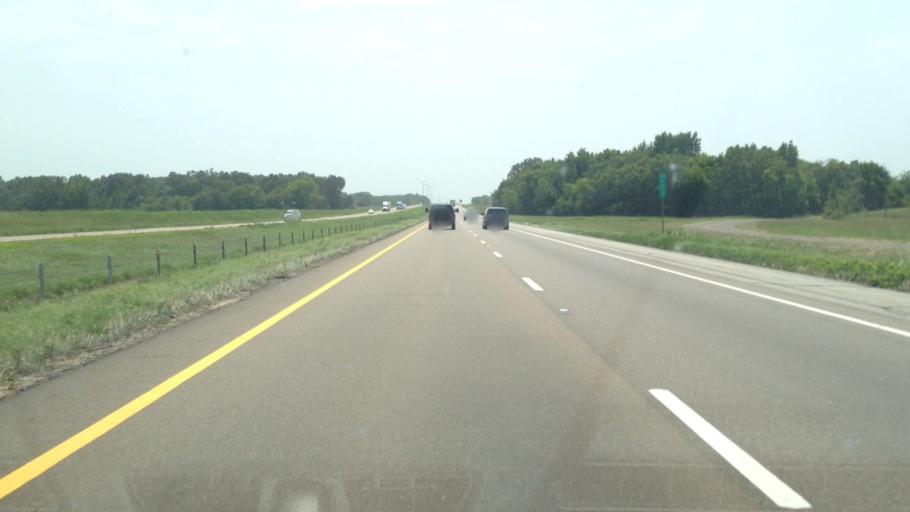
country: US
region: Texas
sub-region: Morris County
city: Omaha
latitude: 33.2496
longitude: -94.8515
